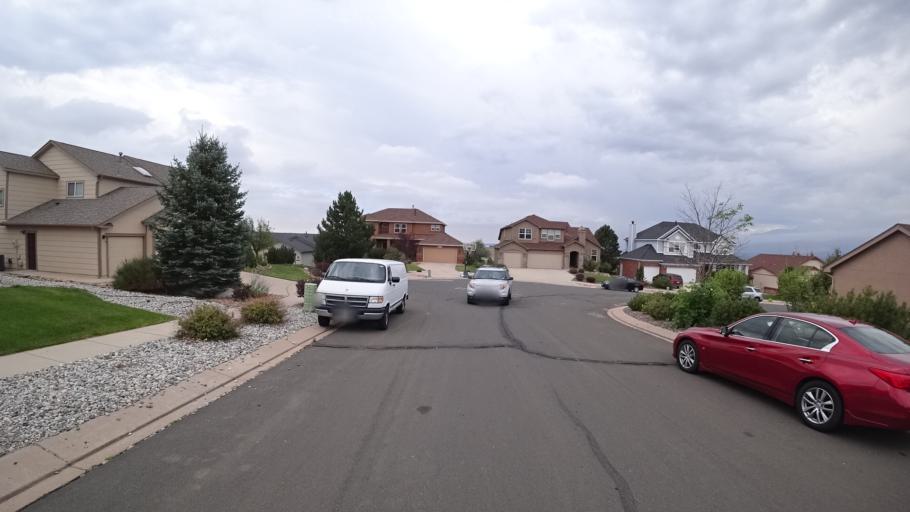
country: US
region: Colorado
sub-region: El Paso County
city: Gleneagle
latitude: 39.0046
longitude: -104.7879
